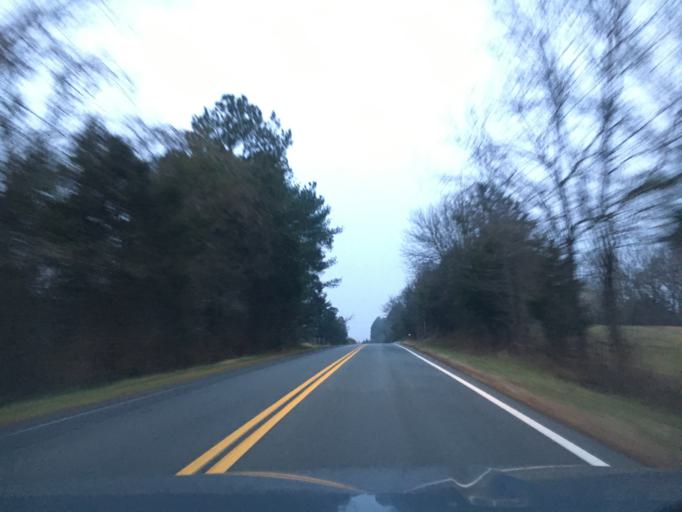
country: US
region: Virginia
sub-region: Halifax County
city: Mountain Road
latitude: 36.6991
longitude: -78.9664
